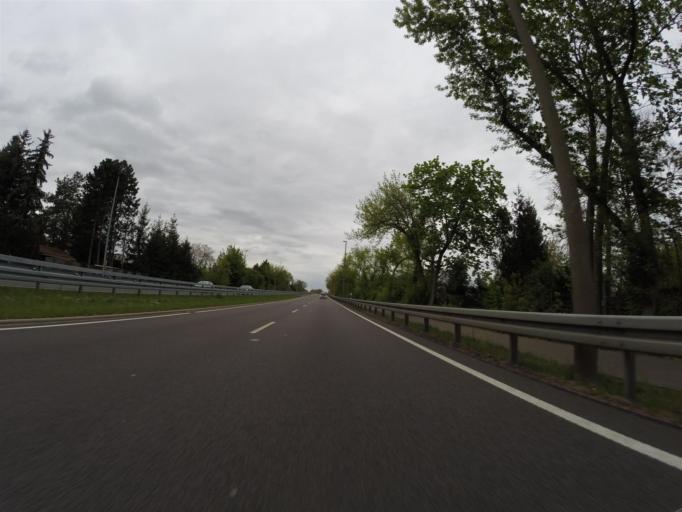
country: DE
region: Saxony-Anhalt
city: Schkopau
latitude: 51.3805
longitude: 11.9816
